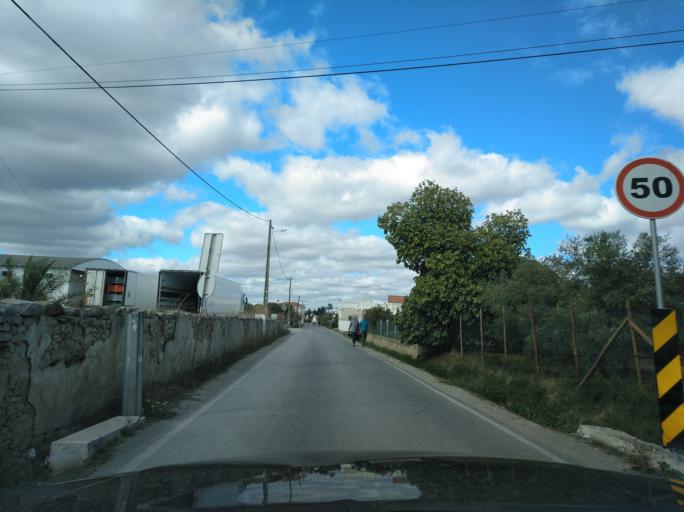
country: PT
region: Faro
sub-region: Tavira
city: Luz
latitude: 37.0953
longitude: -7.7048
